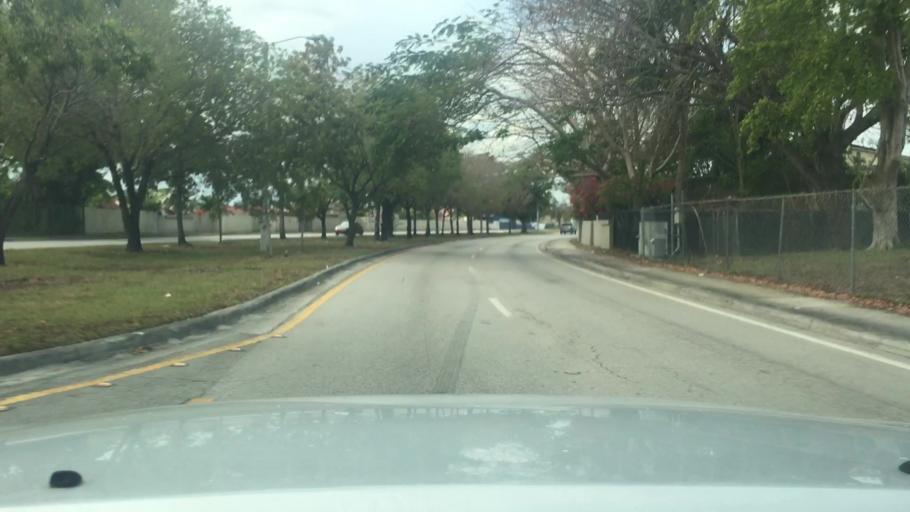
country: US
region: Florida
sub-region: Miami-Dade County
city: Tamiami
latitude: 25.7570
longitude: -80.3922
